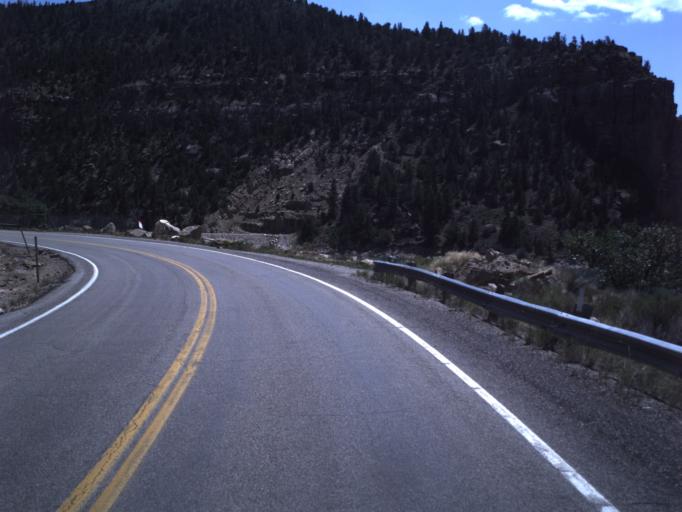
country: US
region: Utah
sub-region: Emery County
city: Orangeville
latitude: 39.2914
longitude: -111.2716
